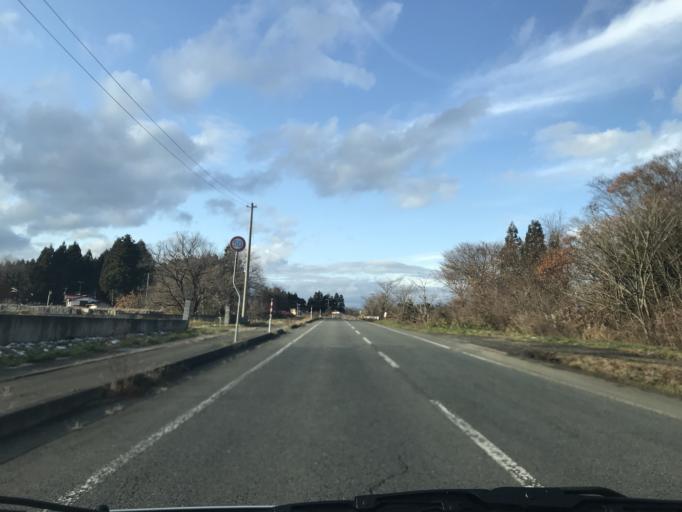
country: JP
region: Iwate
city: Mizusawa
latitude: 39.1934
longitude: 141.0712
